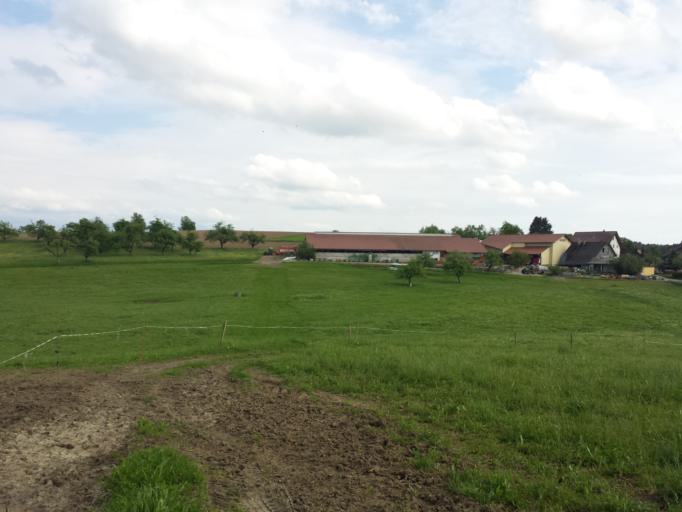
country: DE
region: Baden-Wuerttemberg
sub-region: Tuebingen Region
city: Neukirch
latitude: 47.6623
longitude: 9.7274
